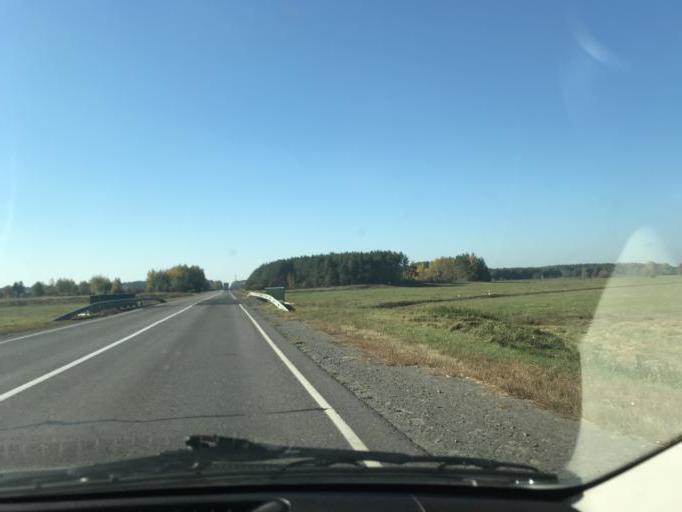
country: BY
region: Brest
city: Davyd-Haradok
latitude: 52.2443
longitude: 27.1509
